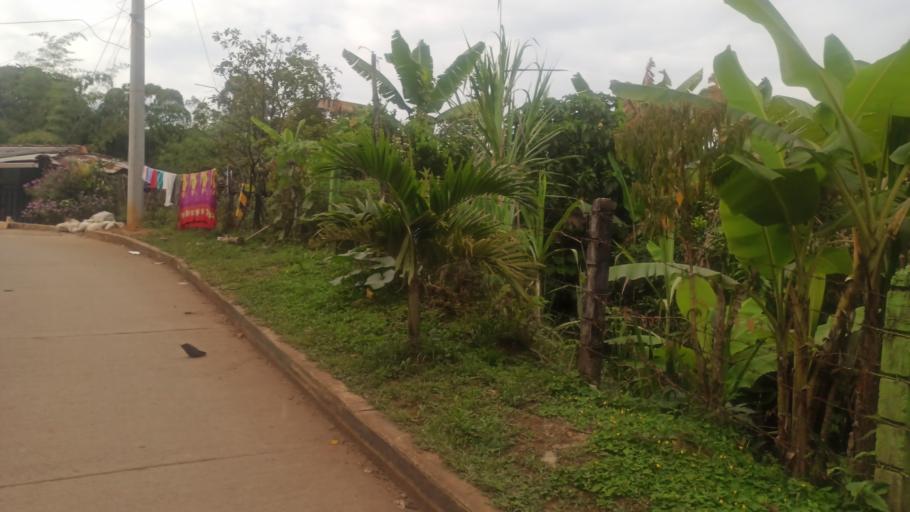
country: CO
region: Valle del Cauca
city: Jamundi
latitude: 3.1861
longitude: -76.6732
